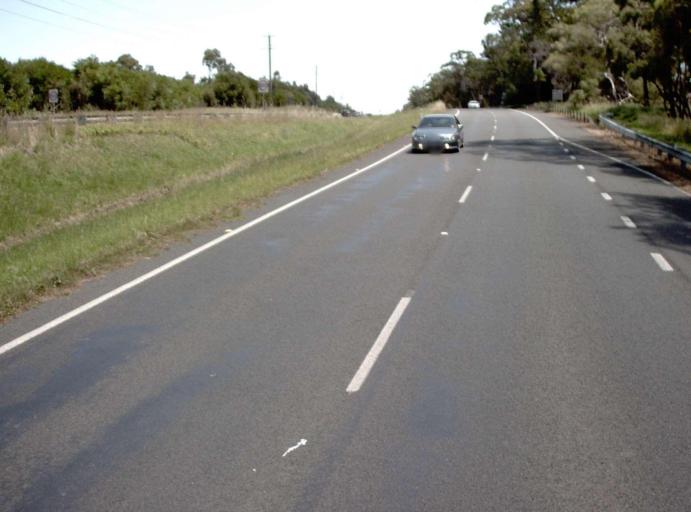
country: AU
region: Victoria
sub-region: Latrobe
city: Traralgon
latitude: -38.2118
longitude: 146.4853
